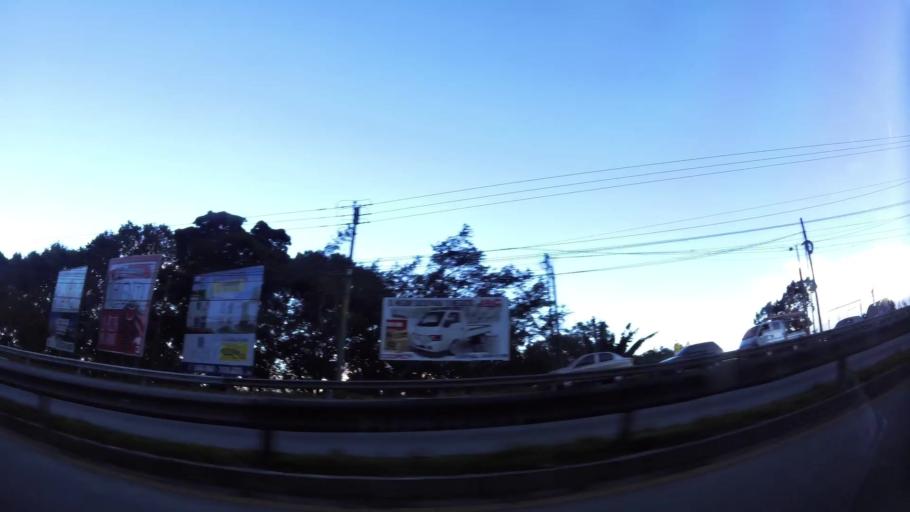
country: GT
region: Sacatepequez
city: San Lucas Sacatepequez
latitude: 14.6016
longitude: -90.6337
